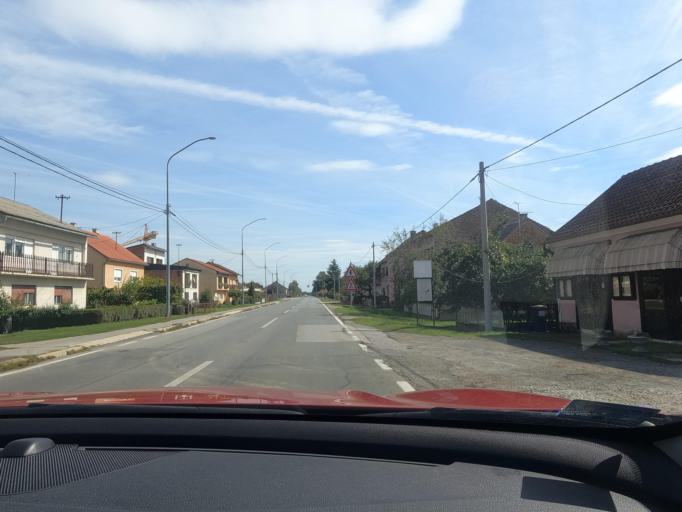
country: HR
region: Sisacko-Moslavacka
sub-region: Grad Sisak
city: Sisak
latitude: 45.4779
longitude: 16.3975
